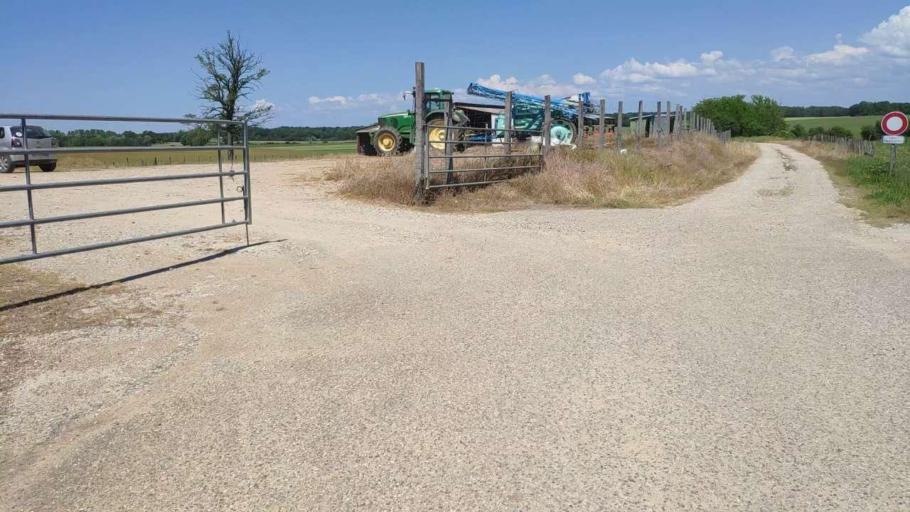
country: FR
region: Franche-Comte
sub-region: Departement du Jura
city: Bletterans
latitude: 46.7444
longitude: 5.3718
